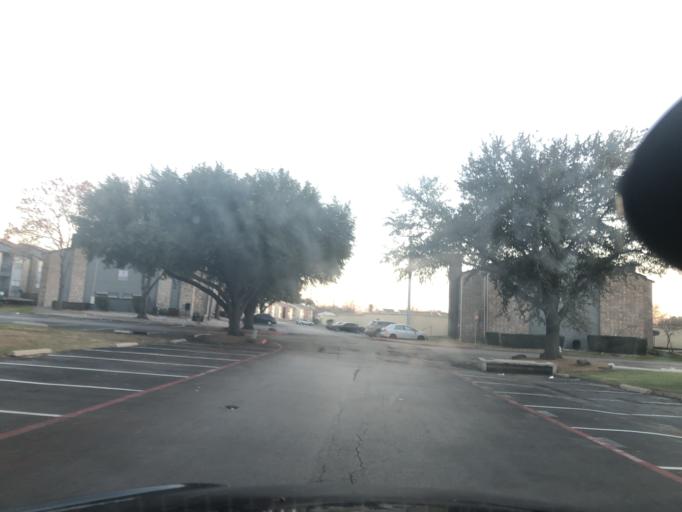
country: US
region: Texas
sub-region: Tarrant County
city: White Settlement
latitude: 32.7354
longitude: -97.4790
